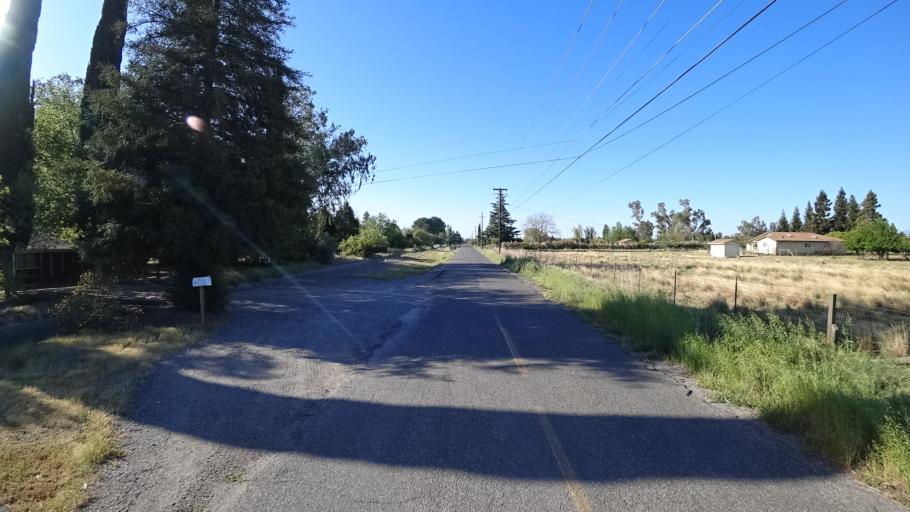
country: US
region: California
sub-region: Glenn County
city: Orland
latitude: 39.7327
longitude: -122.1876
